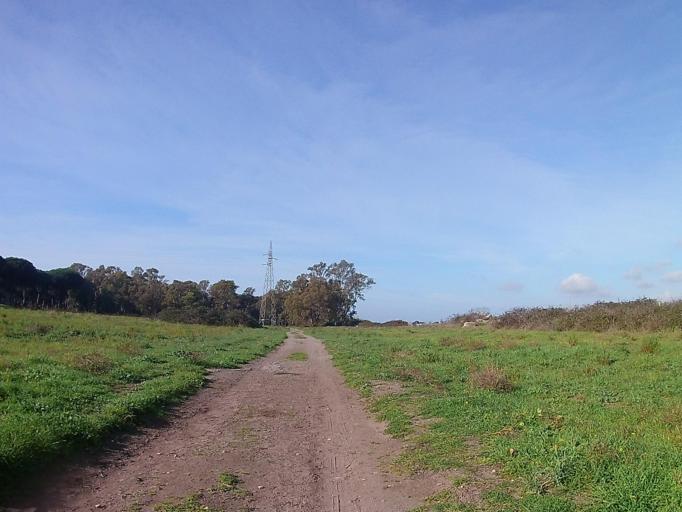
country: IT
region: Latium
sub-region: Citta metropolitana di Roma Capitale
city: Lido di Ostia
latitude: 41.7447
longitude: 12.2844
